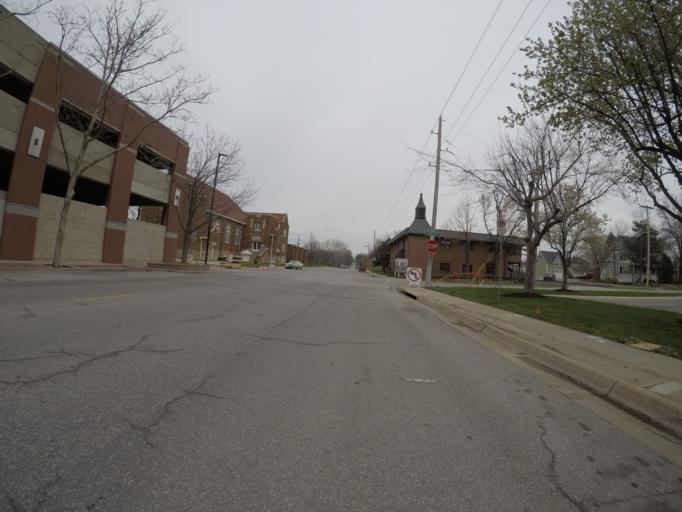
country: US
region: Kansas
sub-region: Johnson County
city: Olathe
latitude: 38.8806
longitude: -94.8187
